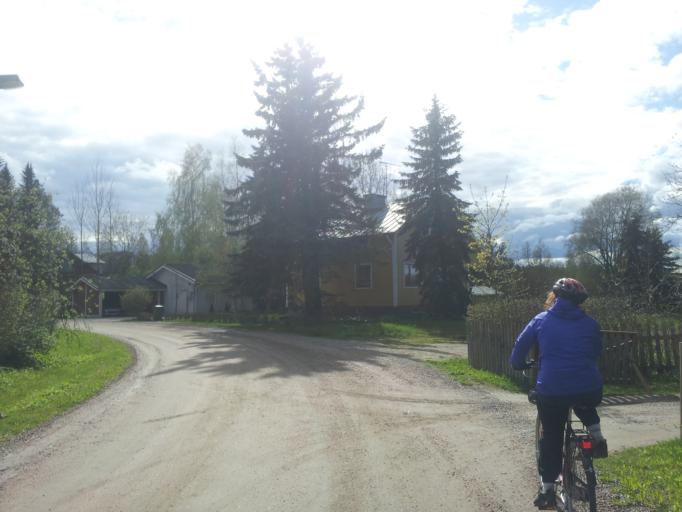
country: FI
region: Haeme
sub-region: Riihimaeki
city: Riihimaeki
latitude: 60.7522
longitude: 24.7758
